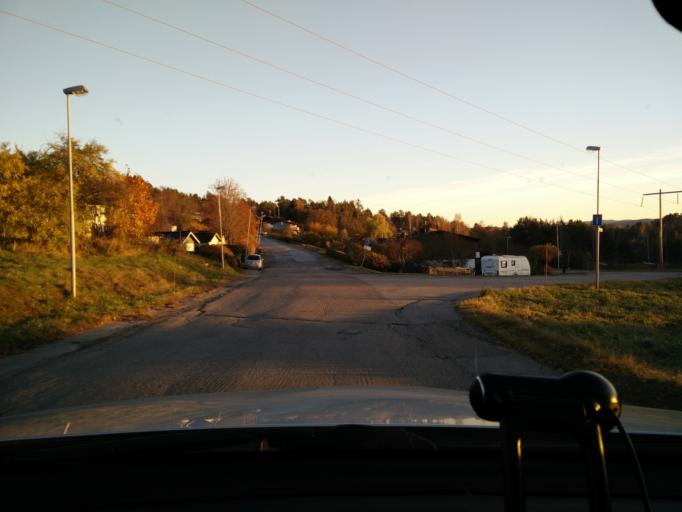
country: SE
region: Vaesternorrland
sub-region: Sundsvalls Kommun
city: Matfors
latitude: 62.3526
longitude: 17.0409
